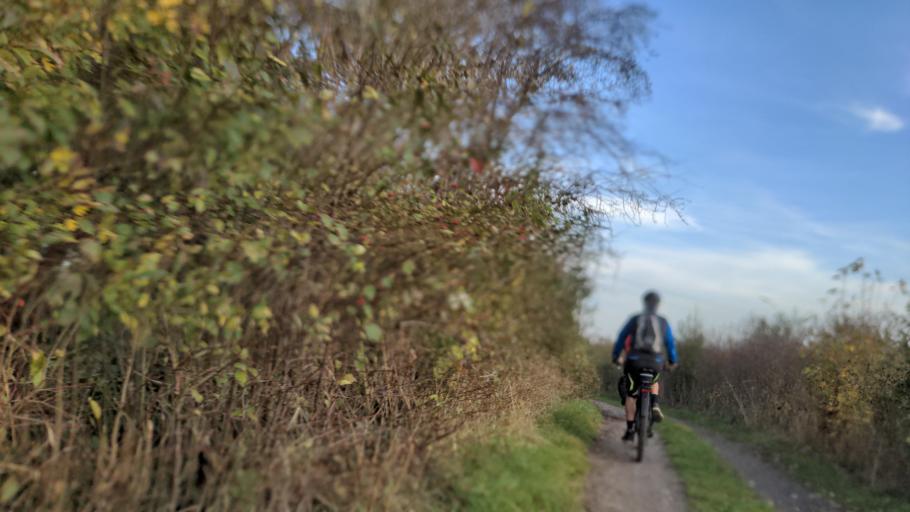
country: DE
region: Schleswig-Holstein
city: Neustadt in Holstein
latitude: 54.1186
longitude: 10.7937
